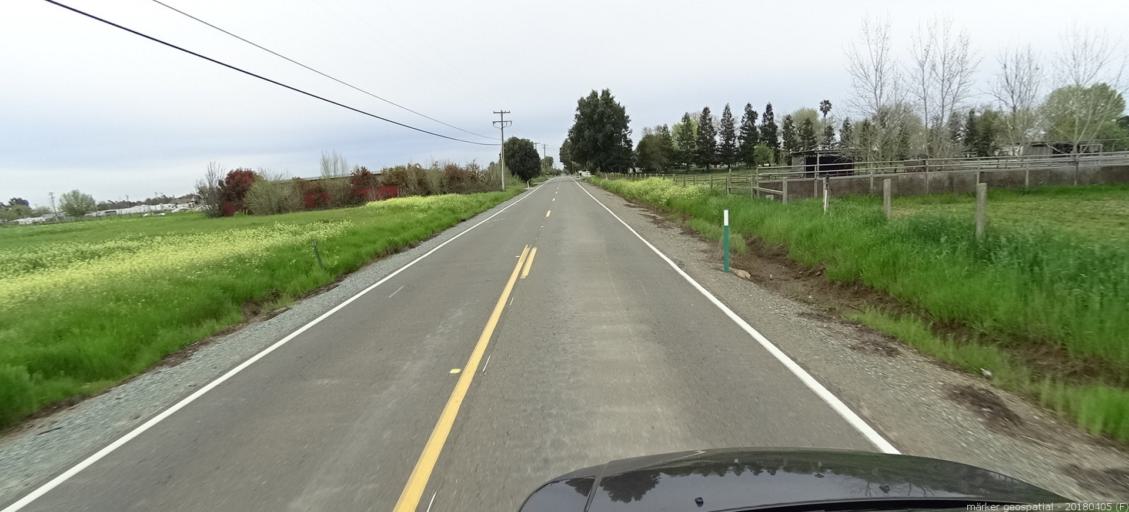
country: US
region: California
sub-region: Sacramento County
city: Herald
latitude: 38.3023
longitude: -121.2264
